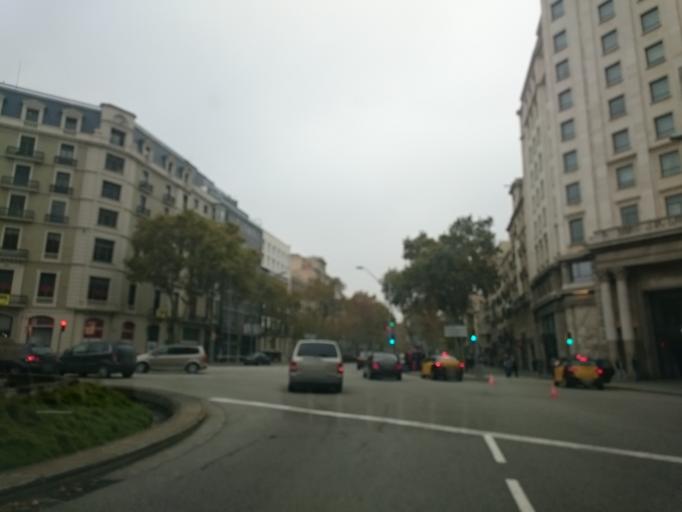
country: ES
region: Catalonia
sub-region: Provincia de Barcelona
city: Eixample
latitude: 41.3893
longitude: 2.1683
